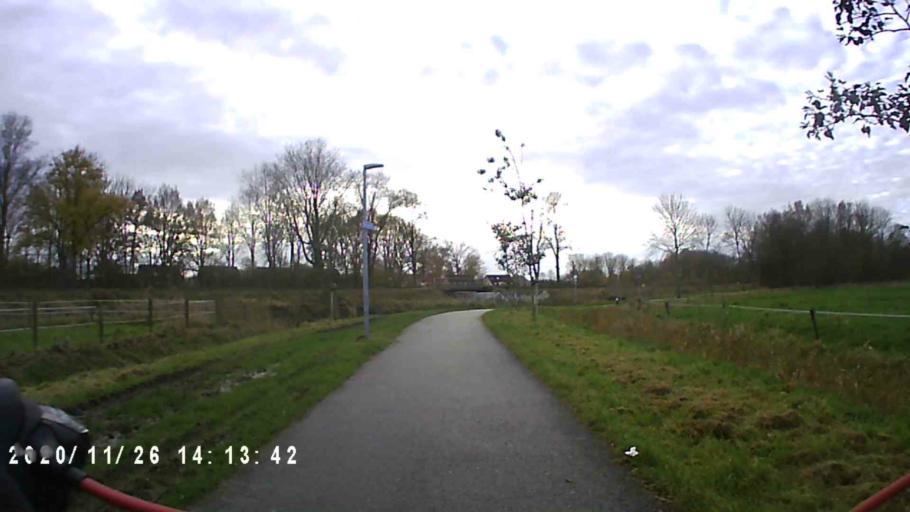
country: NL
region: Groningen
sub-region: Gemeente Delfzijl
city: Delfzijl
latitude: 53.3303
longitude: 6.8925
